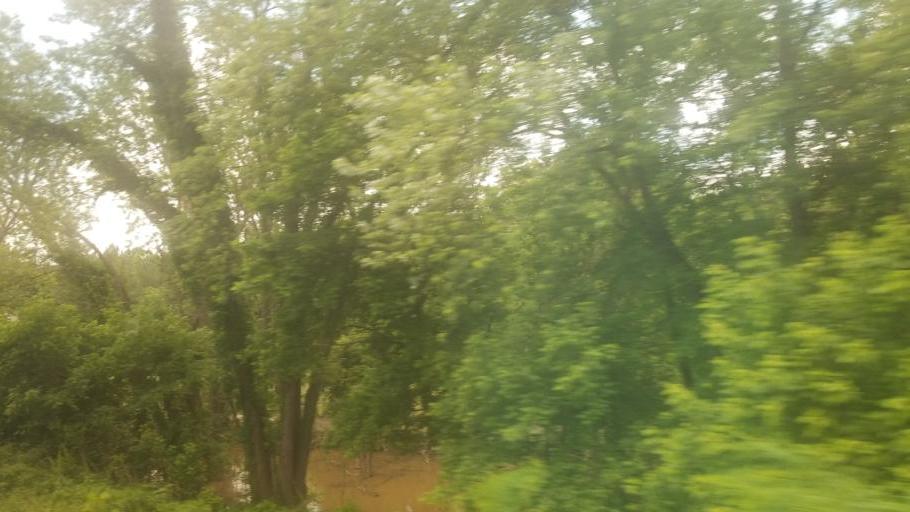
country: US
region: Maryland
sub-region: Frederick County
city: Brunswick
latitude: 39.3096
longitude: -77.6224
